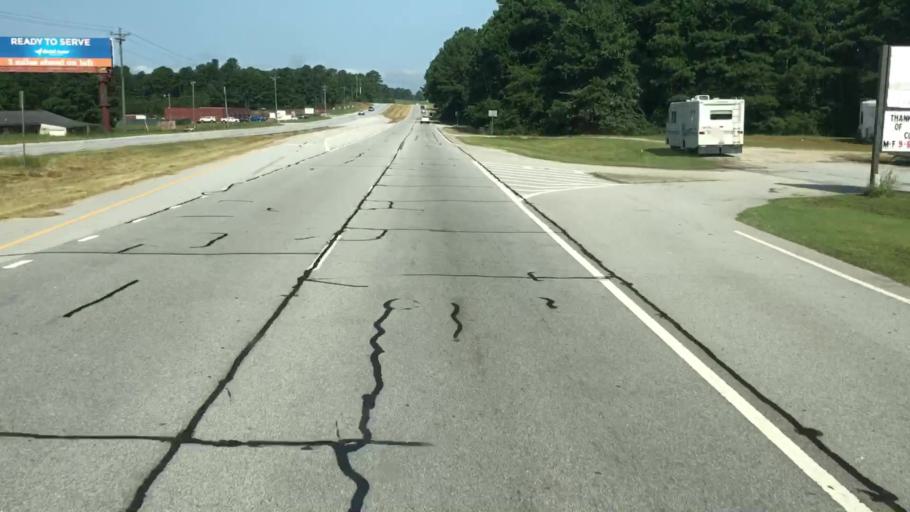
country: US
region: Georgia
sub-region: Walton County
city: Loganville
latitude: 33.8239
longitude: -83.8206
